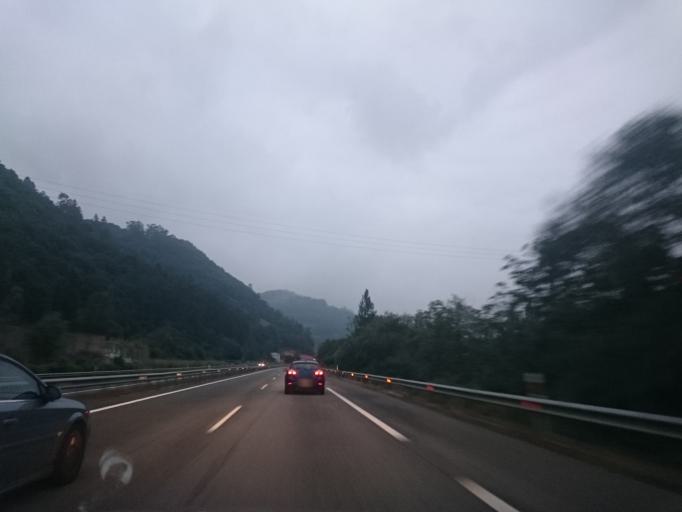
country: ES
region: Asturias
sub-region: Province of Asturias
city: Mieres
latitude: 43.2206
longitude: -5.7840
